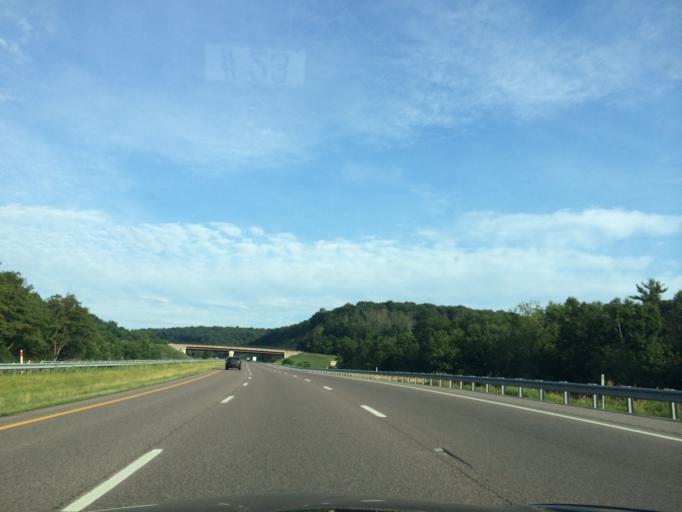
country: US
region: Maryland
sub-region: Allegany County
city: Cumberland
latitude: 39.6931
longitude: -78.5061
